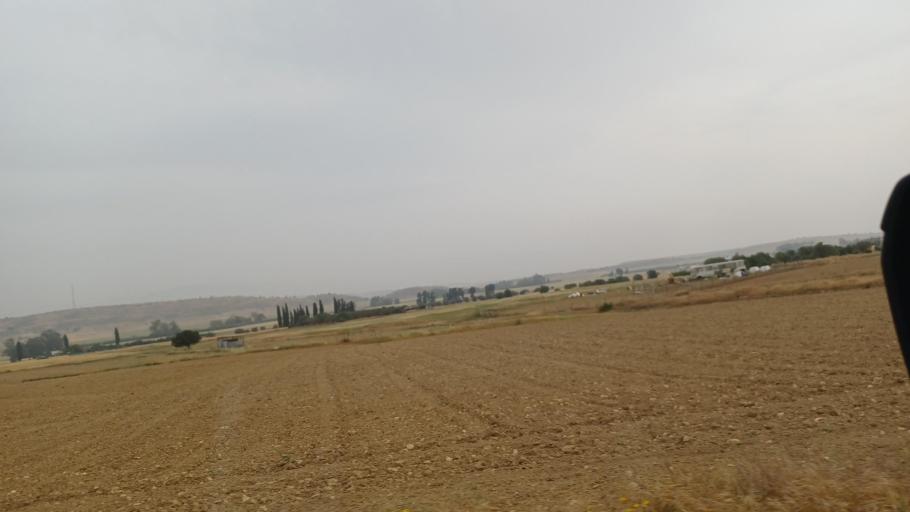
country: CY
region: Lefkosia
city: Mammari
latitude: 35.1791
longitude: 33.1933
